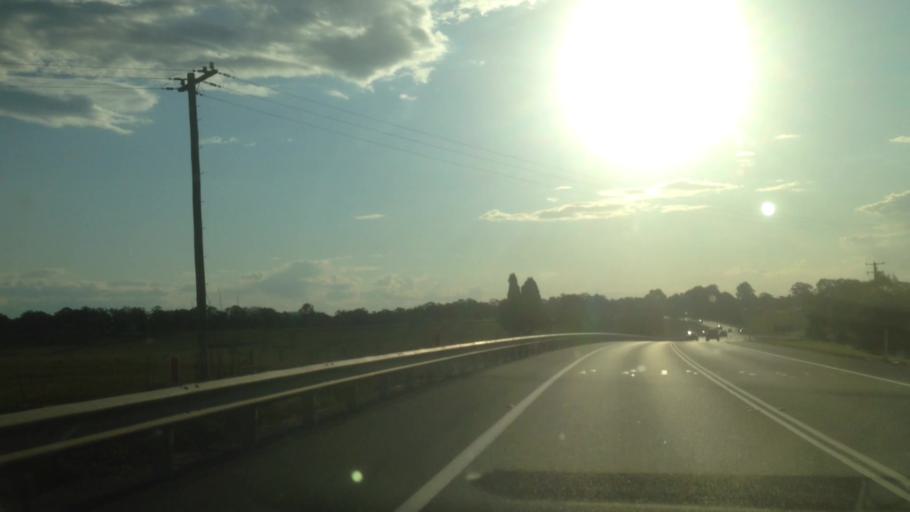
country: AU
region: New South Wales
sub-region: Cessnock
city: Heddon Greta
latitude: -32.8302
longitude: 151.5220
